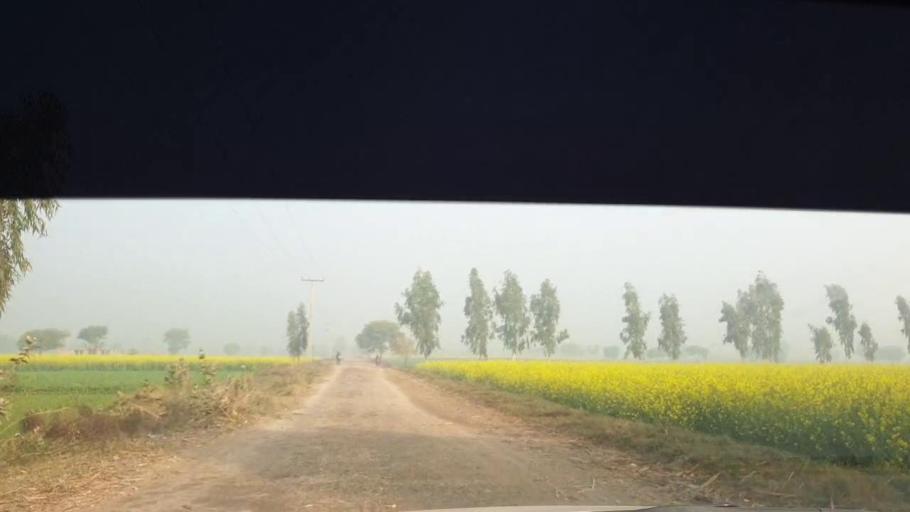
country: PK
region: Sindh
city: Berani
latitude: 25.7902
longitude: 68.7717
